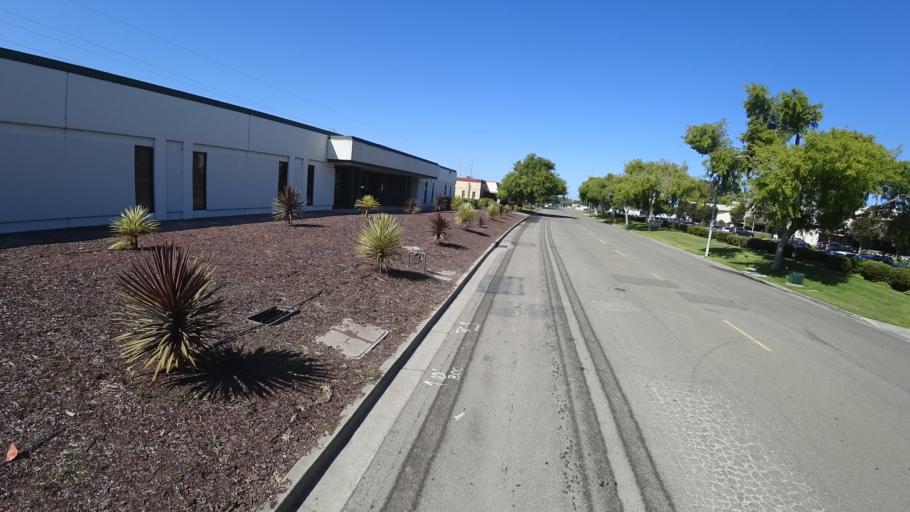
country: US
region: California
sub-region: Alameda County
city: Cherryland
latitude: 37.6270
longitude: -122.1162
